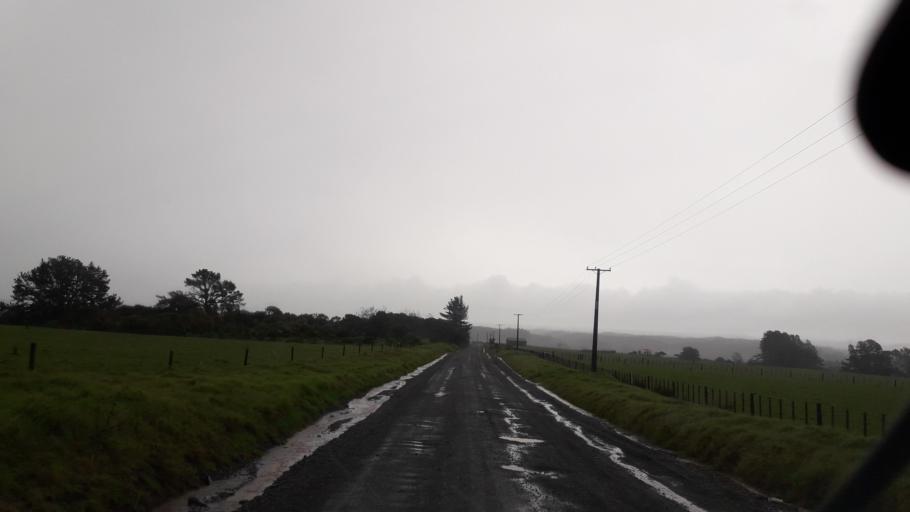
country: NZ
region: Northland
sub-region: Far North District
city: Kerikeri
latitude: -35.1306
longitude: 174.0041
